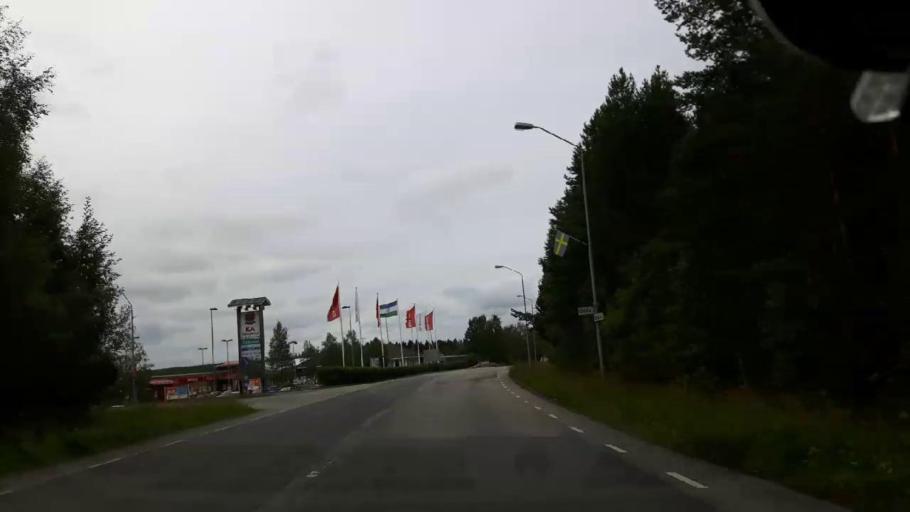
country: SE
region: Jaemtland
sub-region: OEstersunds Kommun
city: Ostersund
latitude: 63.1698
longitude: 14.5674
